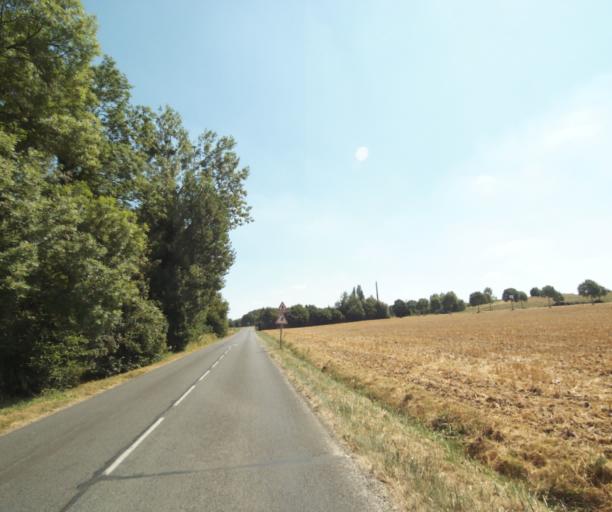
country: FR
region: Ile-de-France
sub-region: Departement de Seine-et-Marne
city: Chanteloup-en-Brie
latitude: 48.8521
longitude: 2.7322
